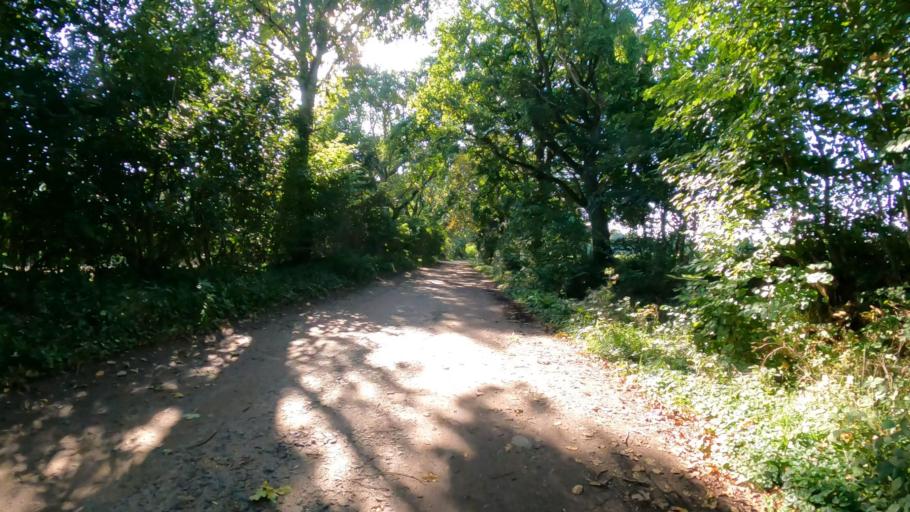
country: DE
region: Schleswig-Holstein
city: Ahrensburg
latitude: 53.6651
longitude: 10.2011
